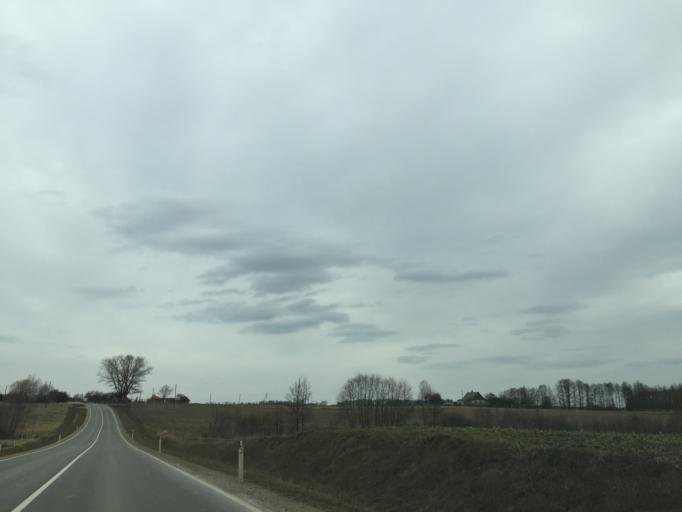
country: LV
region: Ilukste
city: Ilukste
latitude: 55.9885
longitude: 26.2900
